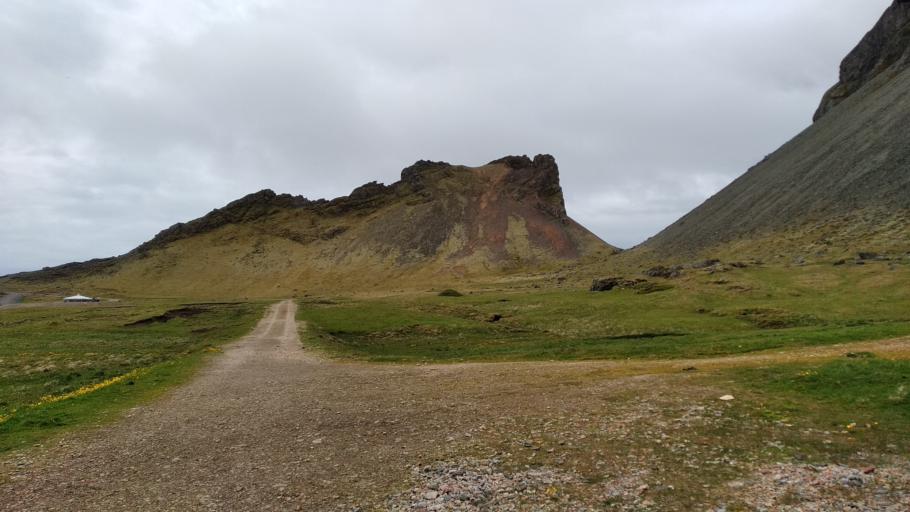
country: IS
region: East
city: Hoefn
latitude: 64.2599
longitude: -14.9875
